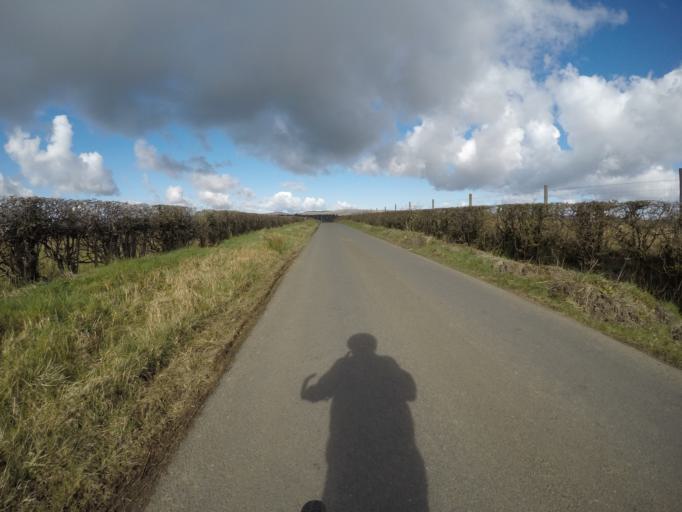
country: GB
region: Scotland
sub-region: North Ayrshire
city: Kilwinning
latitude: 55.6886
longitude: -4.6650
